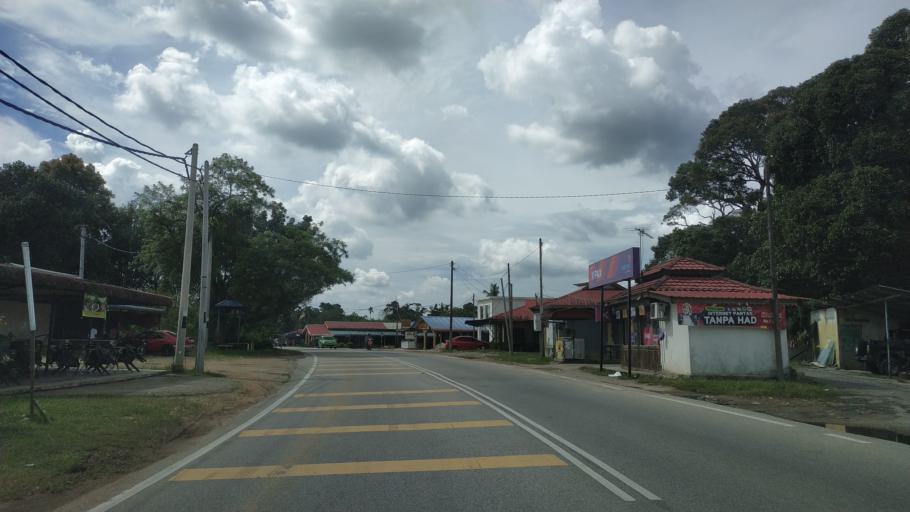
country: MY
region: Kedah
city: Kulim
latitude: 5.4284
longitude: 100.6607
